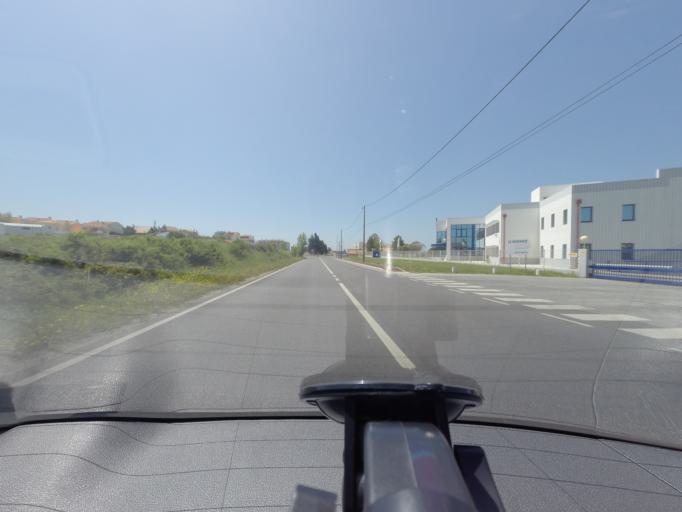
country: PT
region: Lisbon
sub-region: Cascais
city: Parede
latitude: 38.7300
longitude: -9.3604
